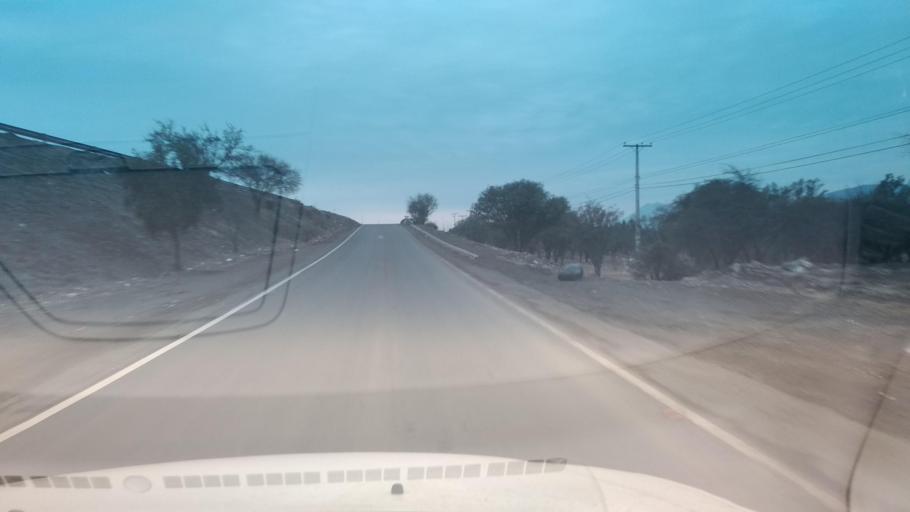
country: CL
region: Santiago Metropolitan
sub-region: Provincia de Chacabuco
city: Chicureo Abajo
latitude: -33.0952
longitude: -70.6931
